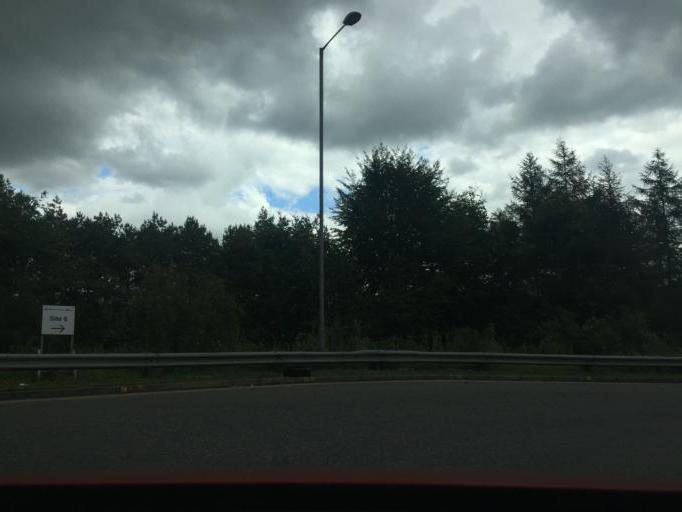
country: GB
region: England
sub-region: Luton
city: Luton
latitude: 51.8705
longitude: -0.3957
